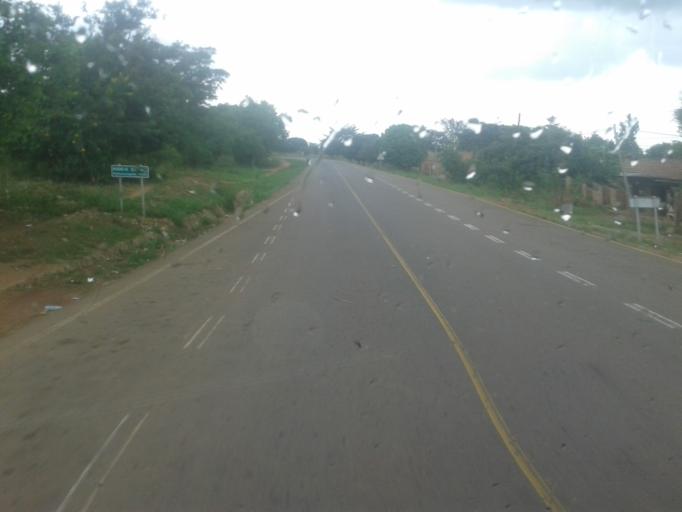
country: UG
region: Central Region
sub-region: Nakasongola District
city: Nakasongola
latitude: 1.3220
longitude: 32.4221
